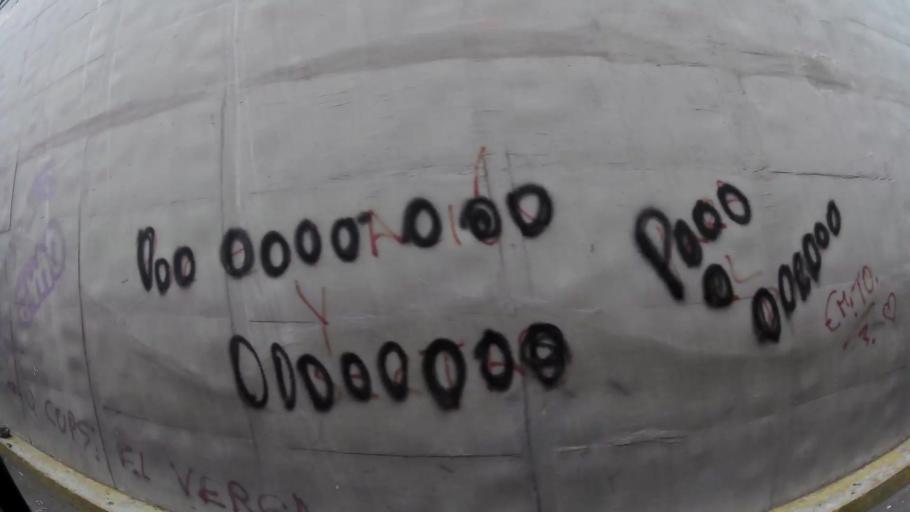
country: EC
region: Cotopaxi
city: Latacunga
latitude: -0.9321
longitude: -78.6221
